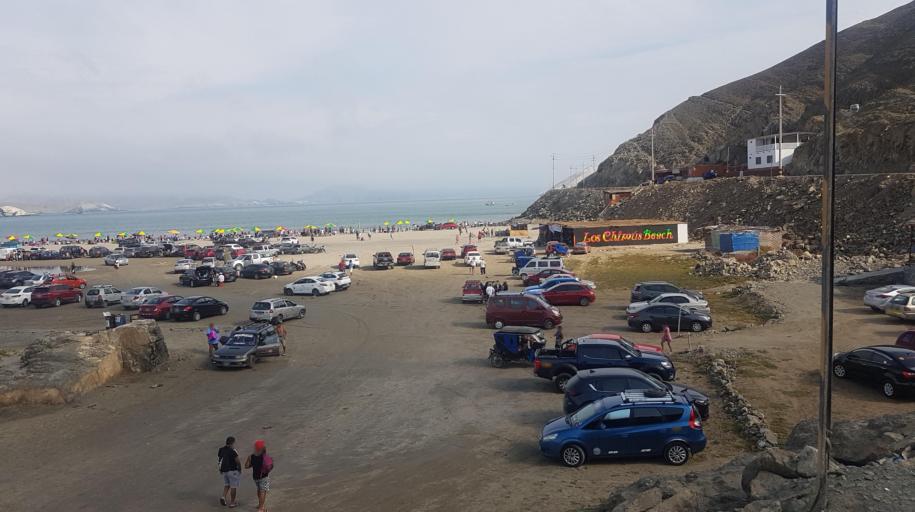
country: PE
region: Ancash
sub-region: Provincia de Santa
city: Samanco
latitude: -9.3218
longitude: -78.4741
